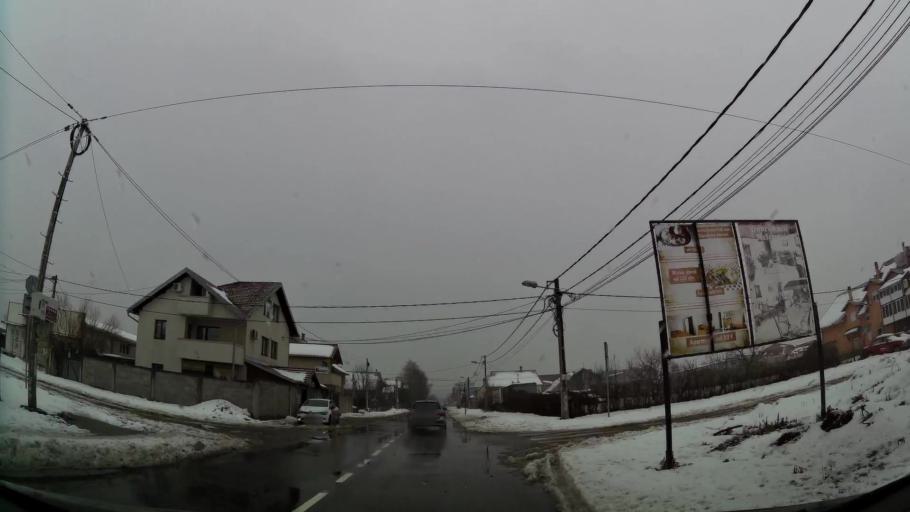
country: RS
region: Central Serbia
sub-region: Belgrade
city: Zemun
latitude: 44.8551
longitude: 20.3441
